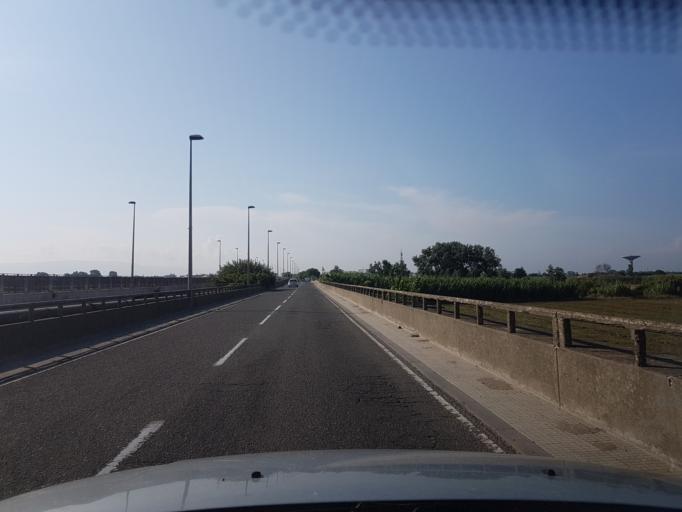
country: IT
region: Sardinia
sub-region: Provincia di Oristano
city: Donigala Fenugheddu
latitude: 39.9204
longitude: 8.5823
